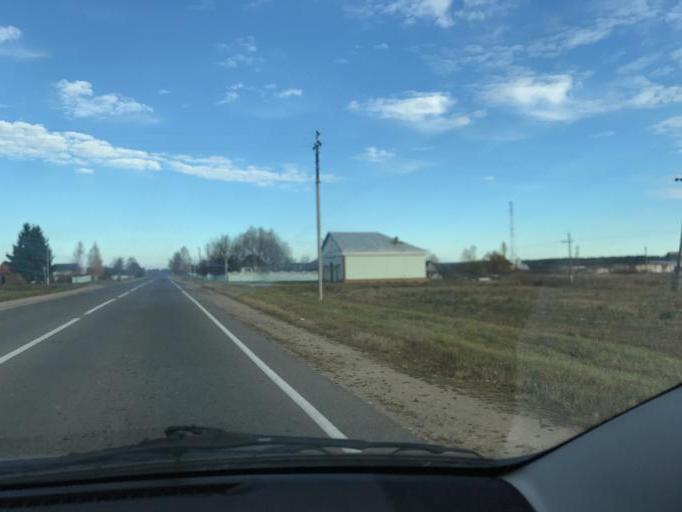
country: BY
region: Vitebsk
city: Haradok
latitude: 55.4834
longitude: 29.9682
